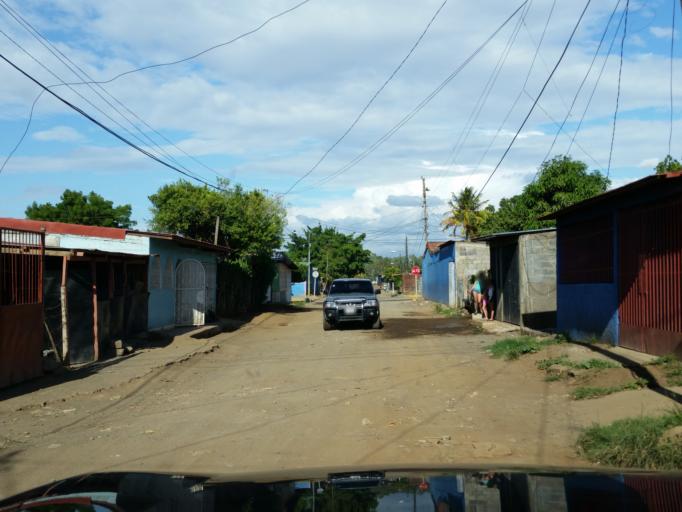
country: NI
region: Managua
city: Managua
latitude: 12.1323
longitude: -86.2774
